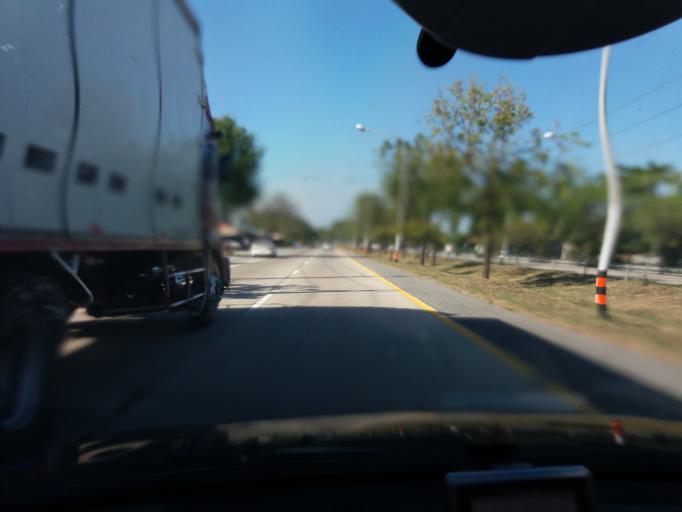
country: TH
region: Suphan Buri
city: Si Prachan
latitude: 14.5854
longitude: 100.1484
